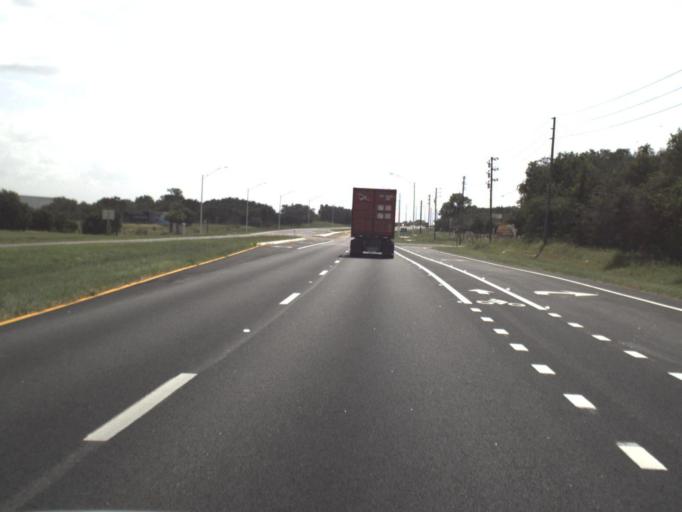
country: US
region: Florida
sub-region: Highlands County
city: Avon Park
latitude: 27.6476
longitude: -81.5315
